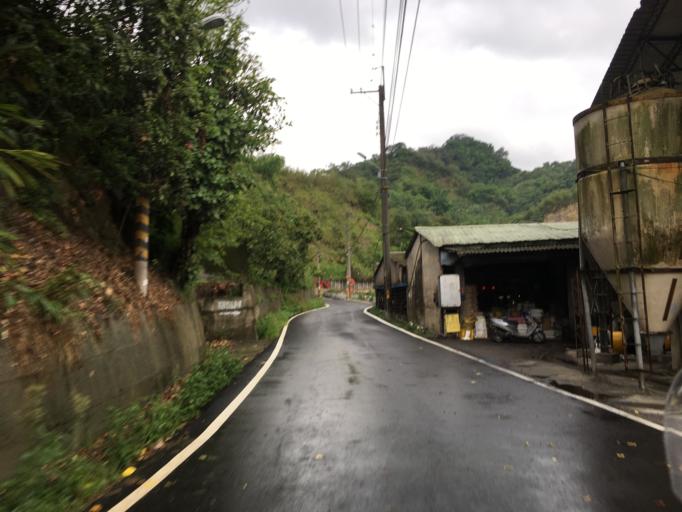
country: TW
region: Taiwan
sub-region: Taichung City
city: Taichung
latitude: 24.0610
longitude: 120.7411
